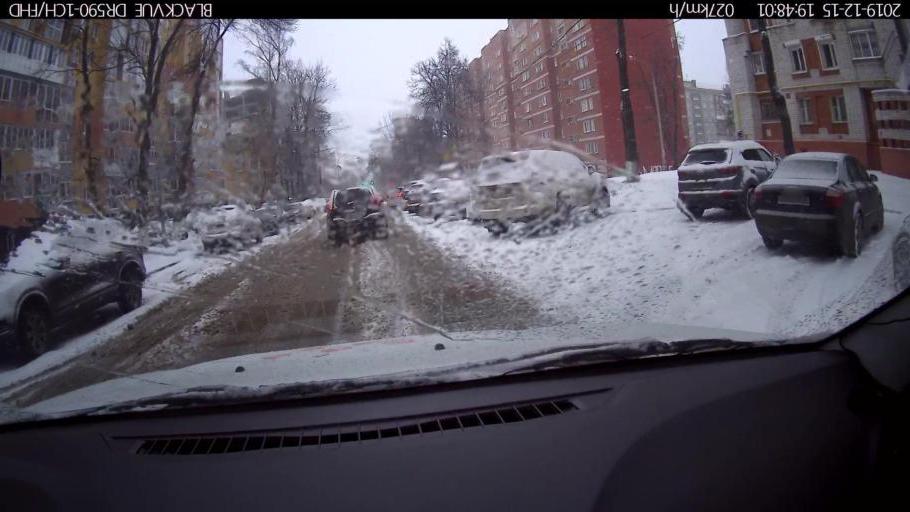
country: RU
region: Nizjnij Novgorod
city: Nizhniy Novgorod
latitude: 56.3147
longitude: 44.0237
